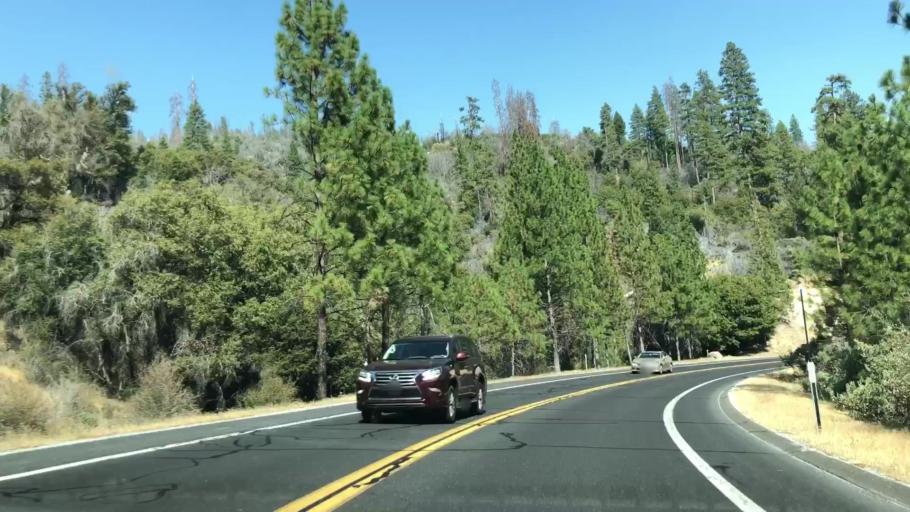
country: US
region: California
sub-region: Mariposa County
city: Midpines
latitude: 37.8189
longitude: -119.9532
